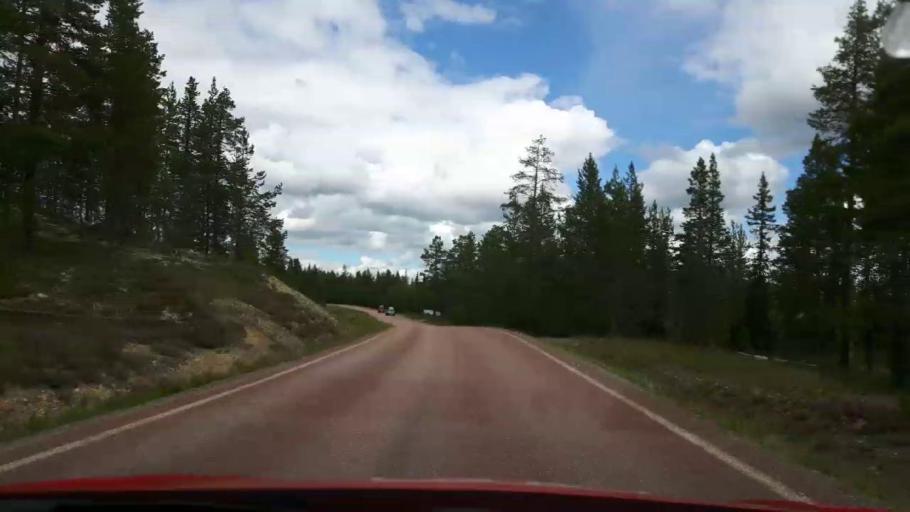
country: NO
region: Hedmark
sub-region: Trysil
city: Innbygda
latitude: 61.8928
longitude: 12.9867
